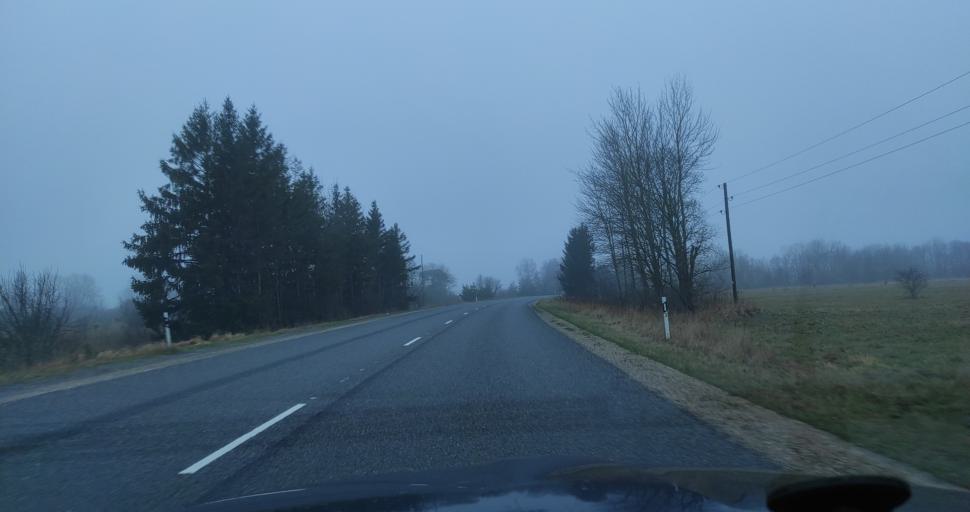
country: LV
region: Alsunga
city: Alsunga
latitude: 57.0009
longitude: 21.3836
